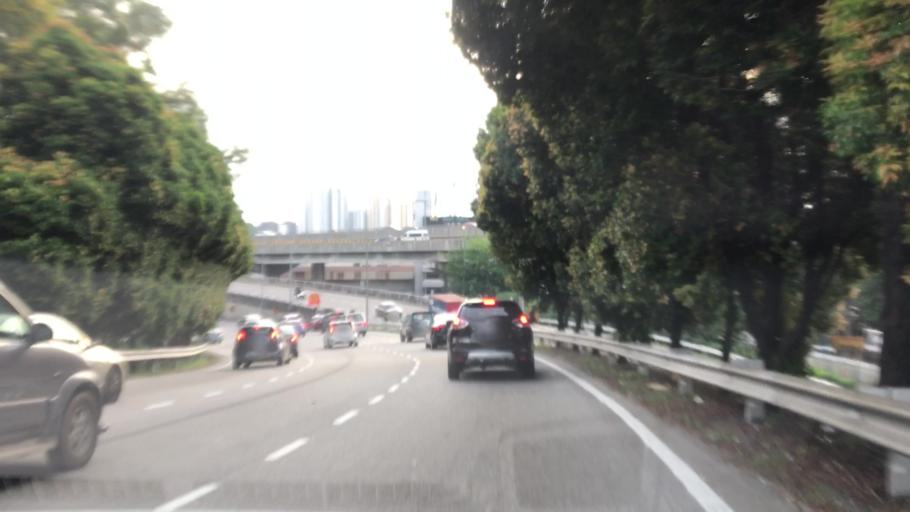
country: MY
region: Kuala Lumpur
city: Kuala Lumpur
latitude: 3.0879
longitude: 101.6960
